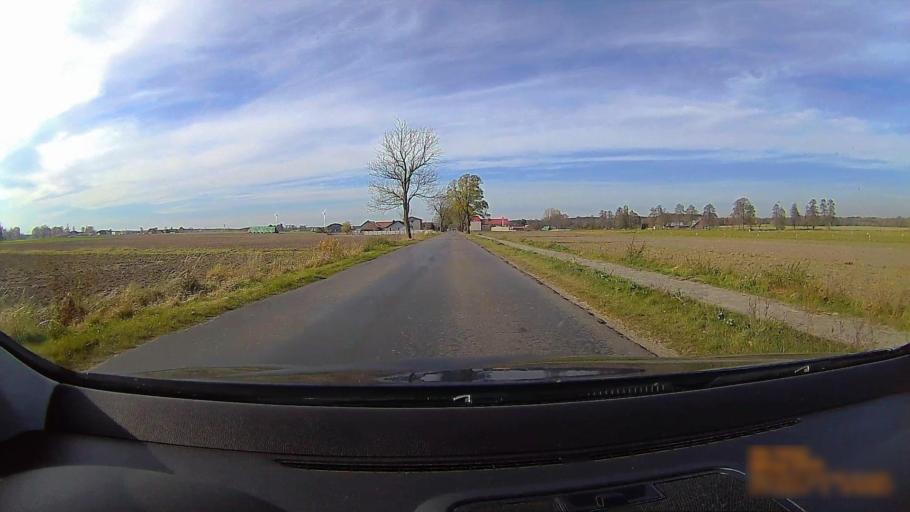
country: PL
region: Greater Poland Voivodeship
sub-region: Powiat ostrzeszowski
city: Doruchow
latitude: 51.4288
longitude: 18.0440
